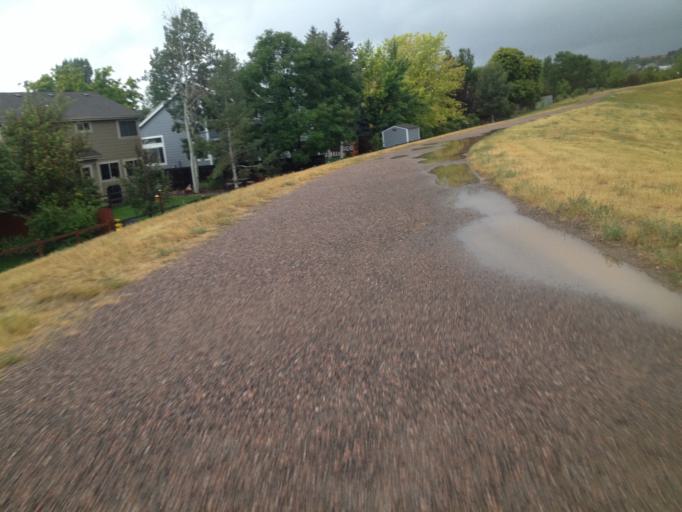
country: US
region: Colorado
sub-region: Boulder County
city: Superior
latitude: 39.9725
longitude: -105.1570
